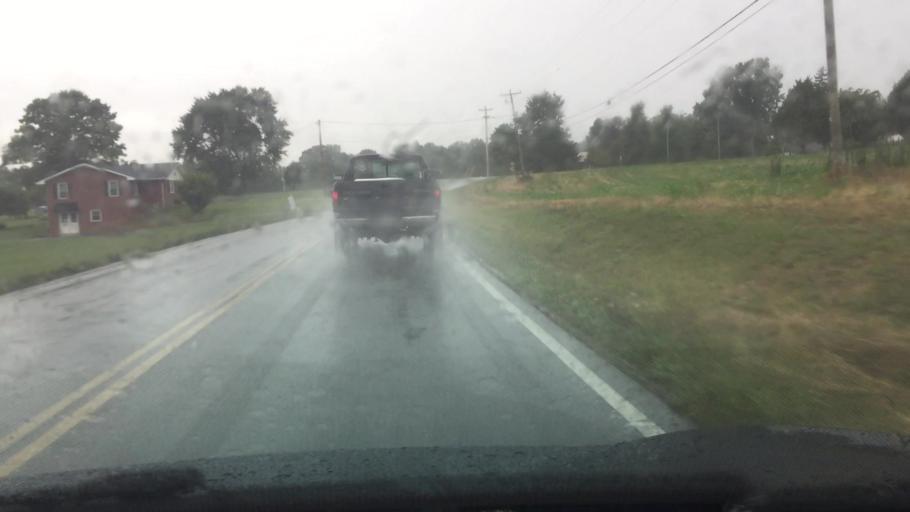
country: US
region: Virginia
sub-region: Campbell County
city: Timberlake
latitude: 37.3104
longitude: -79.3115
